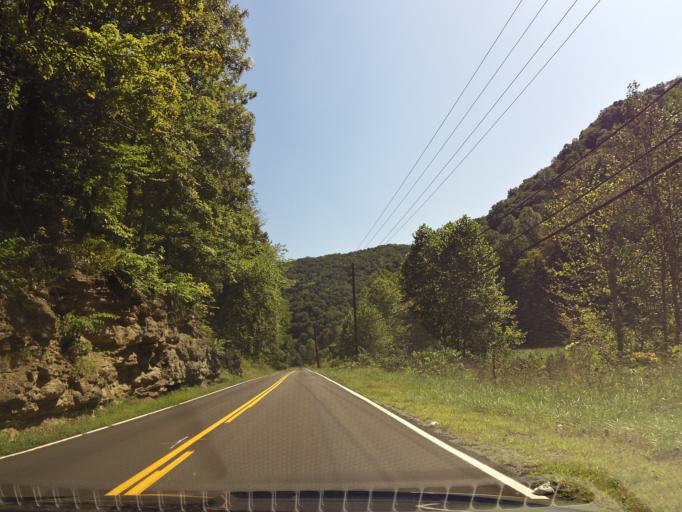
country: US
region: Kentucky
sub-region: Clay County
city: Manchester
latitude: 37.1168
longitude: -83.6461
